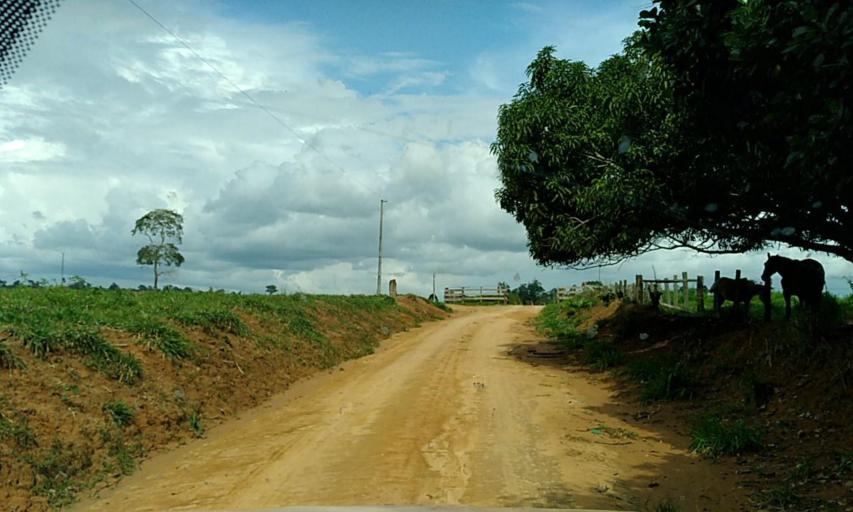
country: BR
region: Para
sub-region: Altamira
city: Altamira
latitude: -3.2363
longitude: -52.7431
